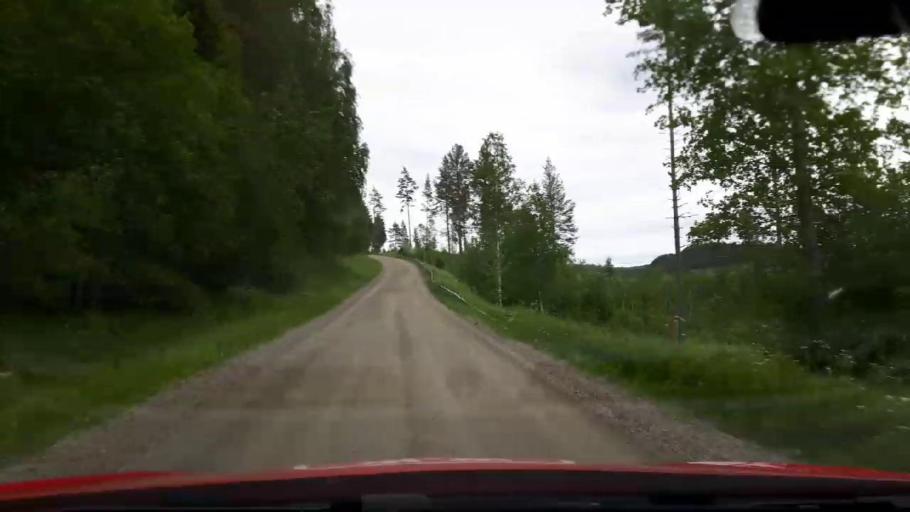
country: SE
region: Jaemtland
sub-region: Ragunda Kommun
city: Hammarstrand
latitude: 63.1837
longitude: 16.1498
